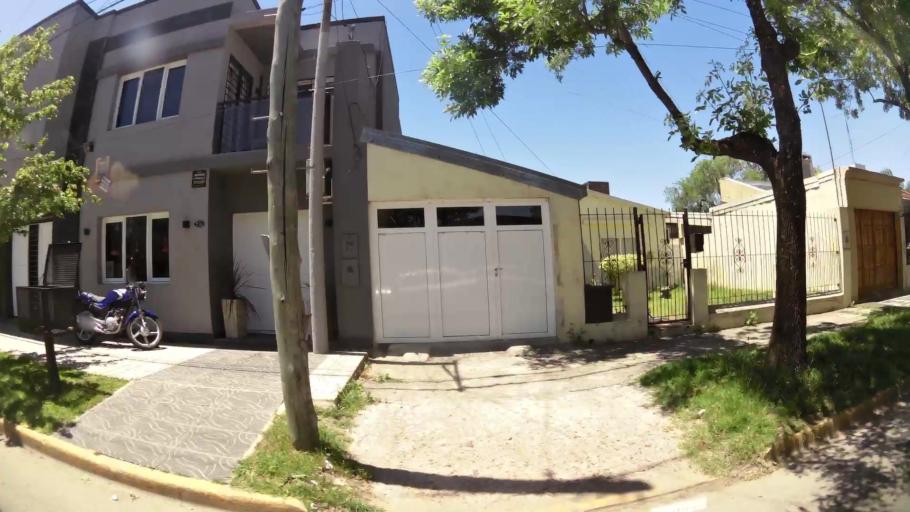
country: AR
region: Santa Fe
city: Rafaela
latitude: -31.2550
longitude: -61.4641
